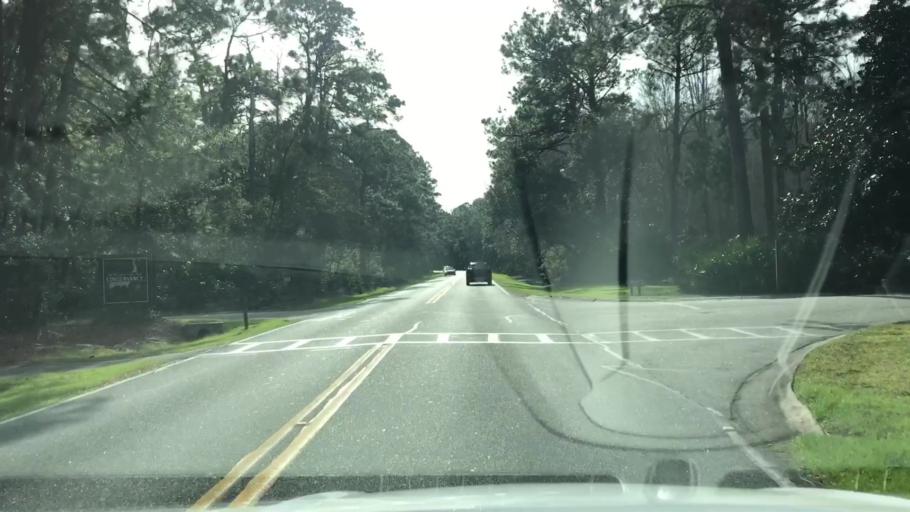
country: US
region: South Carolina
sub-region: Beaufort County
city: Hilton Head Island
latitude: 32.2374
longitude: -80.7222
